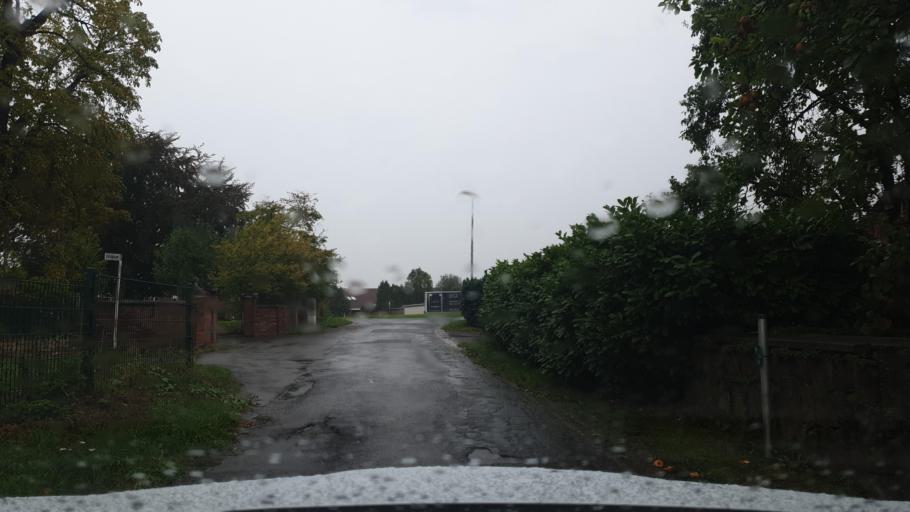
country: DE
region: North Rhine-Westphalia
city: Porta Westfalica
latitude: 52.2177
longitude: 8.8704
